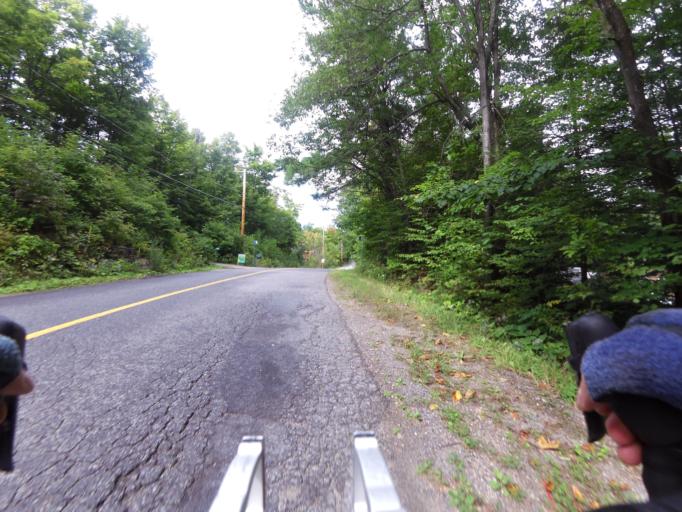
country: CA
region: Quebec
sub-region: Outaouais
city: Gatineau
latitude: 45.5470
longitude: -75.7426
